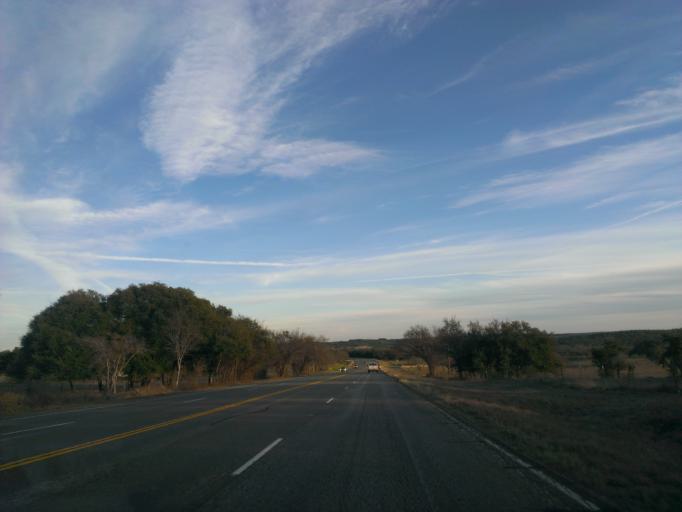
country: US
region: Texas
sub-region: Lampasas County
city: Kempner
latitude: 30.9316
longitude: -98.0093
